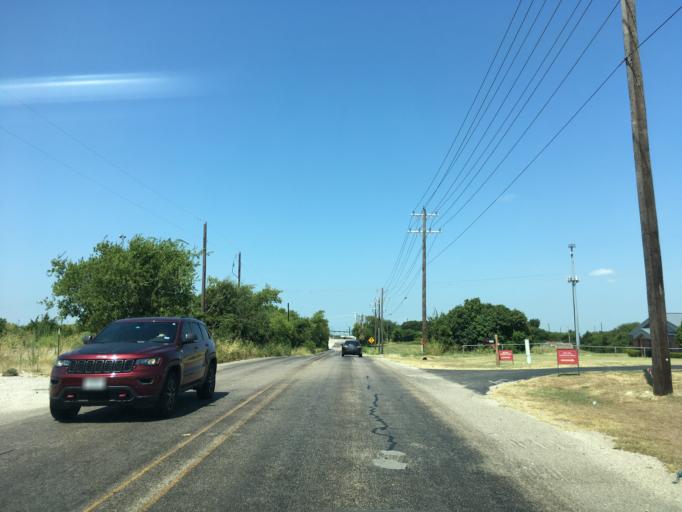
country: US
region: Texas
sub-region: Collin County
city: Prosper
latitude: 33.2041
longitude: -96.7983
